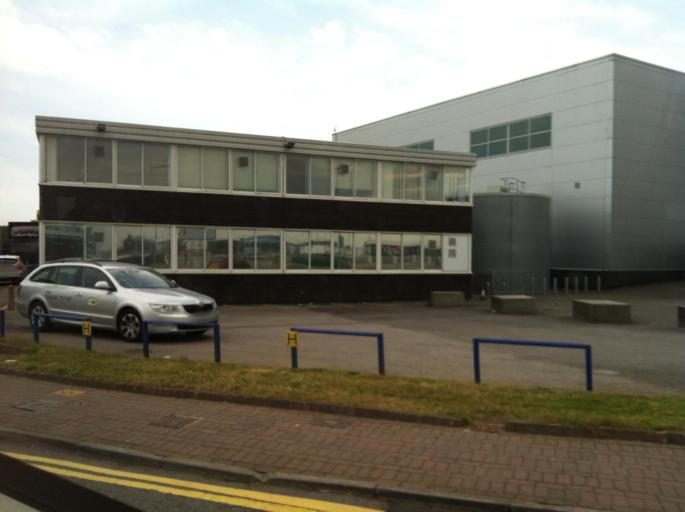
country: GB
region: Wales
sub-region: Vale of Glamorgan
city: Rhoose
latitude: 51.3992
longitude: -3.3384
